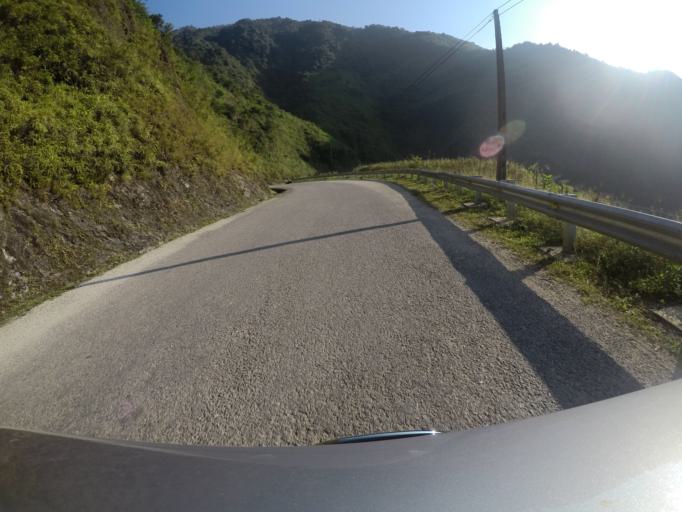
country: VN
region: Lai Chau
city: Than Uyen
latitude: 22.0380
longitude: 103.9480
